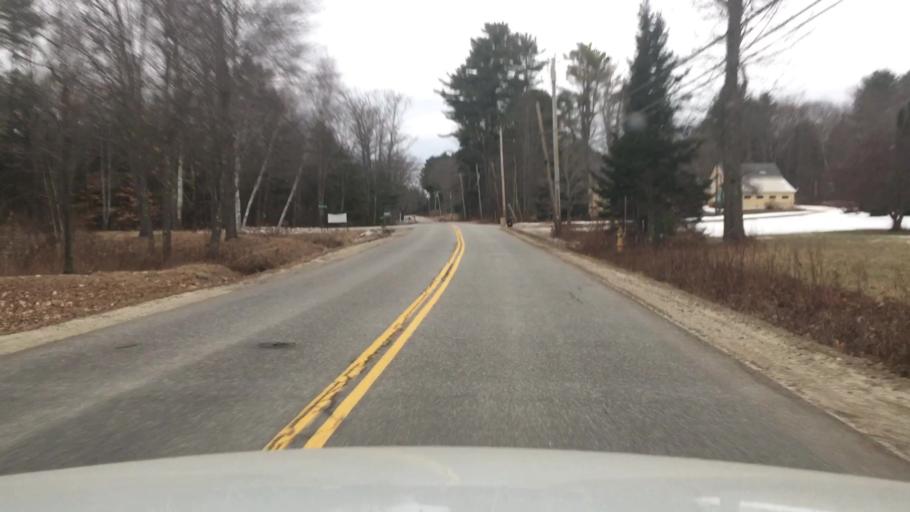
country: US
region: Maine
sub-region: Cumberland County
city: Brunswick
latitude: 43.8948
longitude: -70.0024
